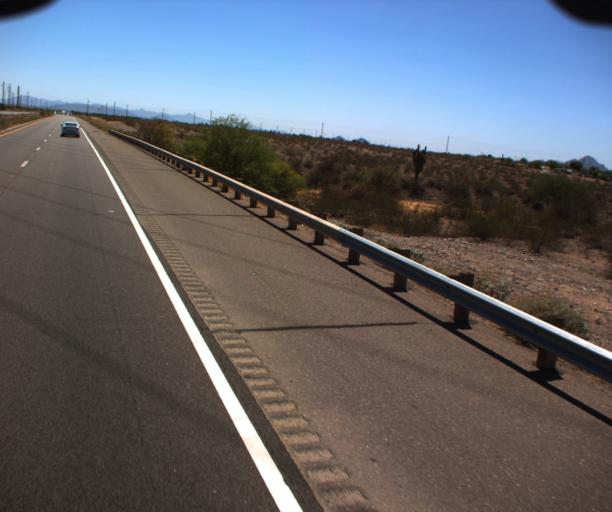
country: US
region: Arizona
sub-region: Maricopa County
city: Mesa
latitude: 33.4988
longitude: -111.8008
